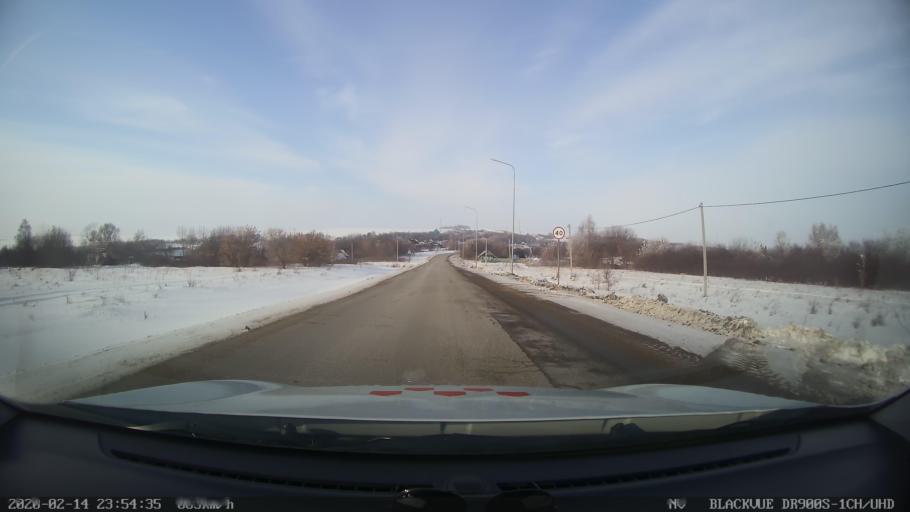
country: RU
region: Tatarstan
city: Kuybyshevskiy Zaton
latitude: 55.3098
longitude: 49.1463
